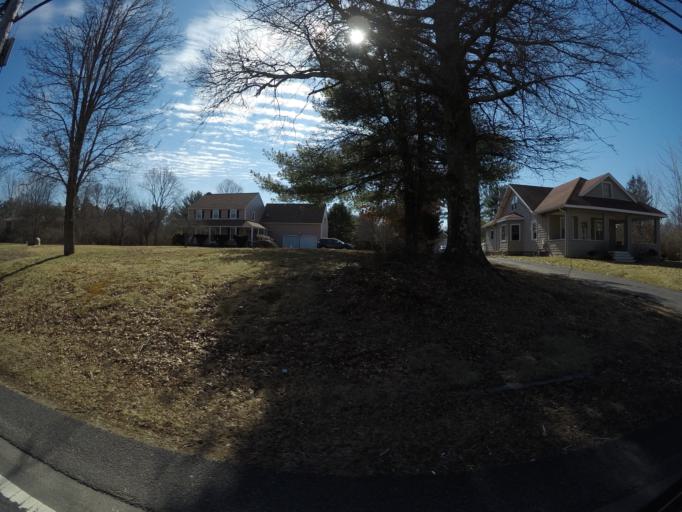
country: US
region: Massachusetts
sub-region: Bristol County
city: Easton
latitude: 42.0677
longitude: -71.1166
